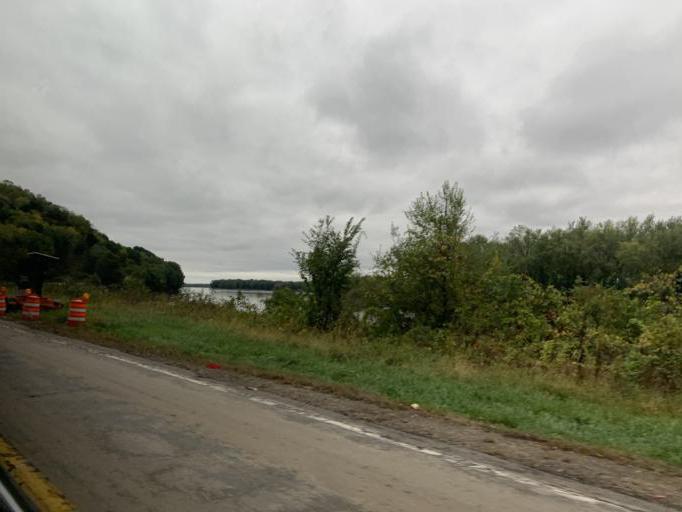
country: US
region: Wisconsin
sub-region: Grant County
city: Muscoda
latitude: 43.2112
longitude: -90.3565
